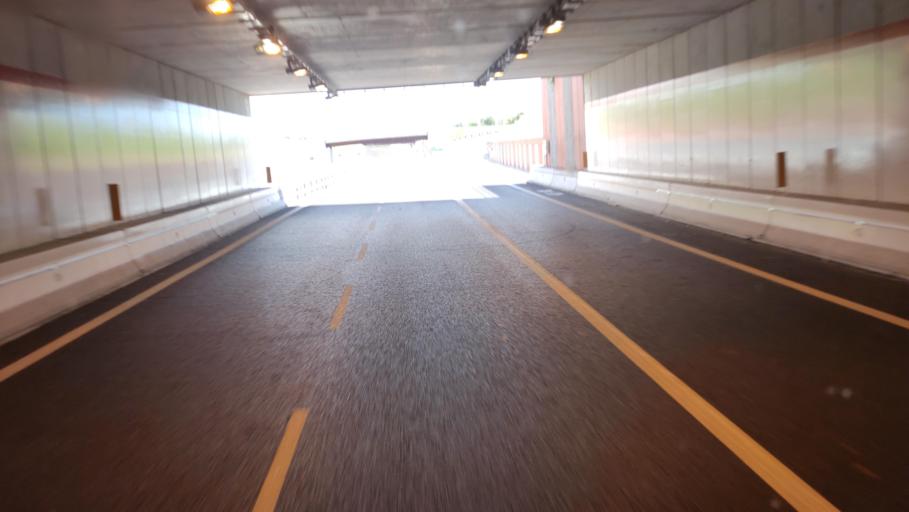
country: IT
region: Veneto
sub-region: Provincia di Treviso
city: Ca' Rainati
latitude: 45.7490
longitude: 11.8590
